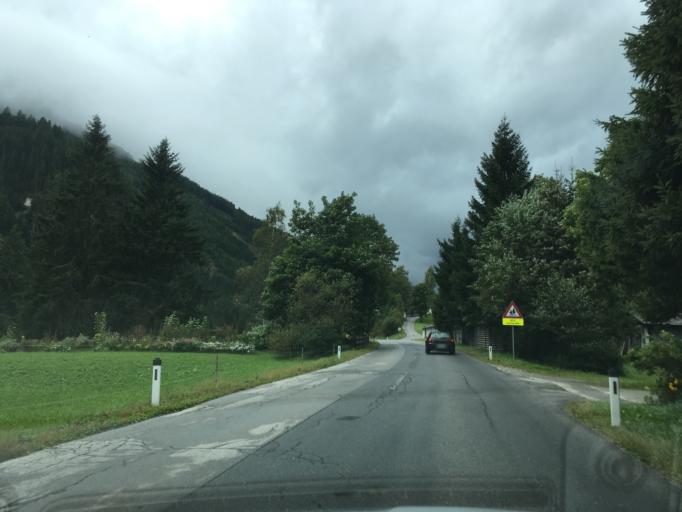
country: AT
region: Tyrol
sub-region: Politischer Bezirk Lienz
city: Virgen
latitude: 46.9189
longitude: 12.4110
